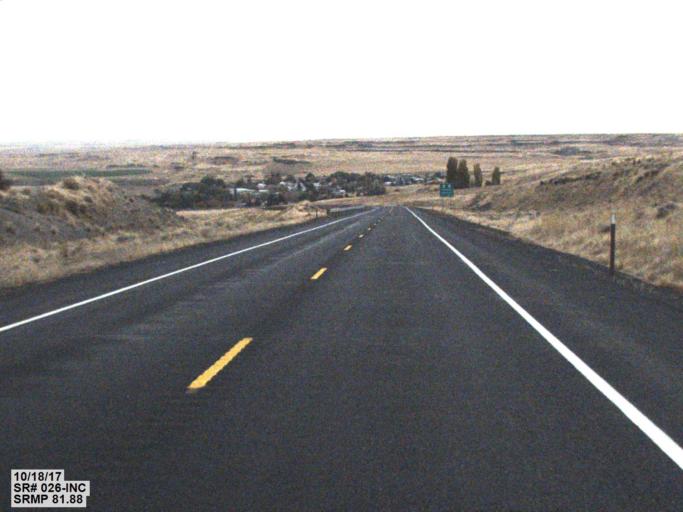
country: US
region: Washington
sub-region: Adams County
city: Ritzville
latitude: 46.7624
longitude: -118.3301
